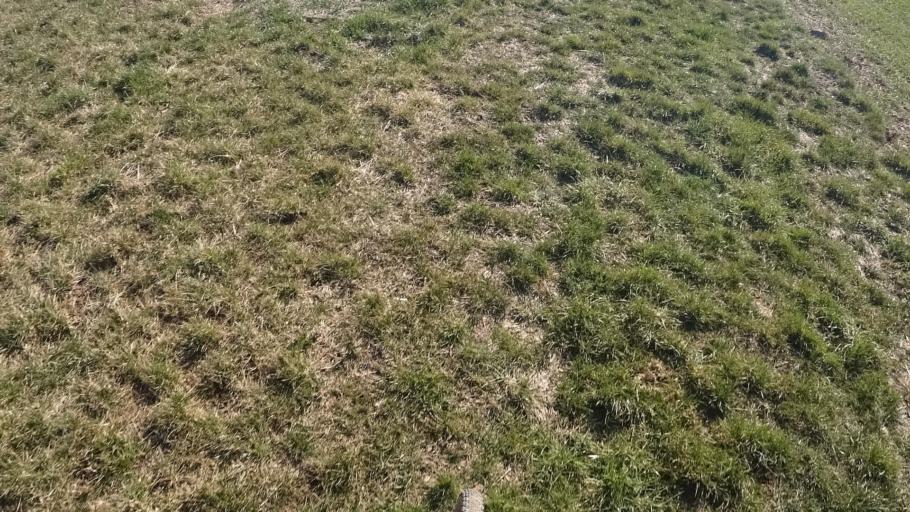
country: DE
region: Rheinland-Pfalz
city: Mutterschied
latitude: 49.9861
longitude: 7.5645
